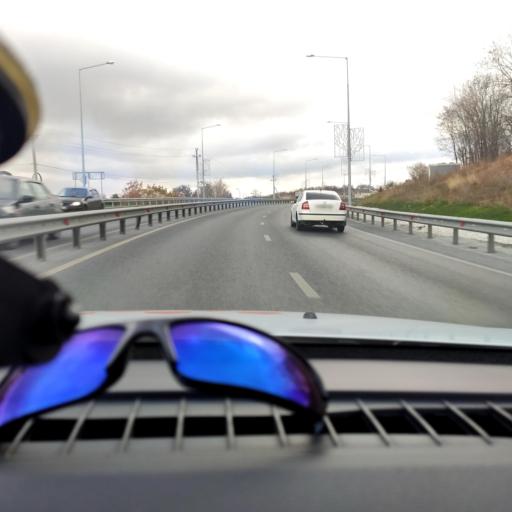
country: RU
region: Samara
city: Volzhskiy
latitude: 53.3692
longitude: 50.1916
